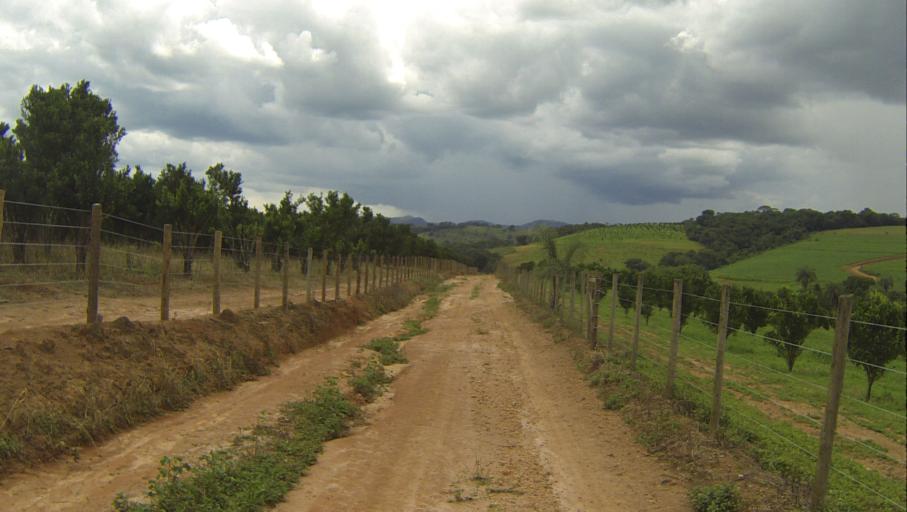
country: BR
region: Minas Gerais
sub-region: Brumadinho
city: Brumadinho
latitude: -20.1526
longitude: -44.1229
